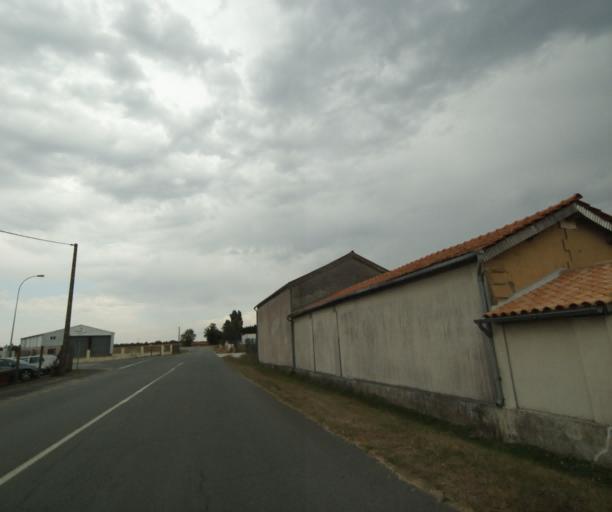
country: FR
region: Poitou-Charentes
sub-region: Departement de la Charente-Maritime
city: Tonnay-Charente
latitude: 45.9522
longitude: -0.8875
